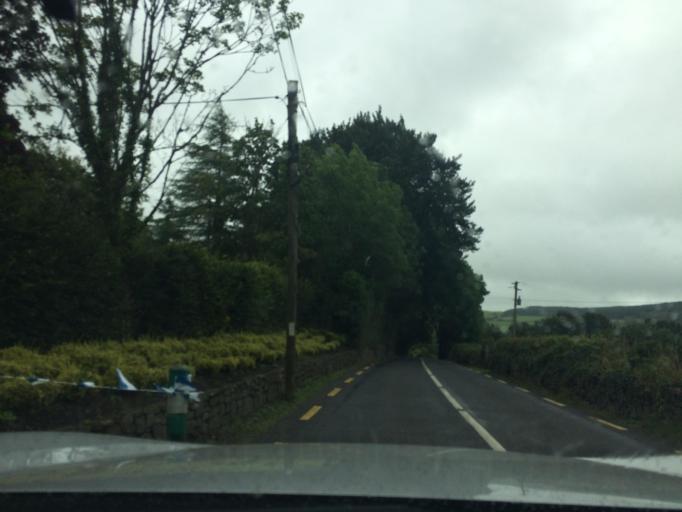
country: IE
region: Munster
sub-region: South Tipperary
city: Cluain Meala
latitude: 52.2760
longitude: -7.7304
